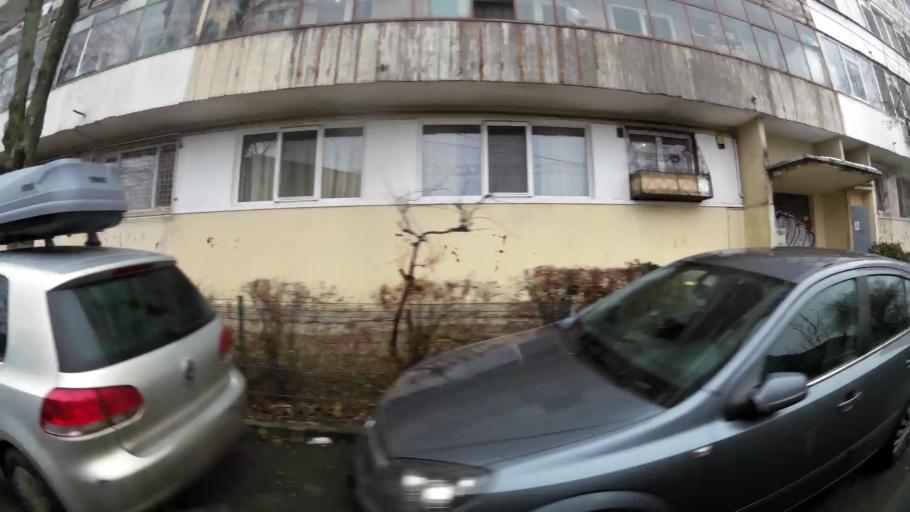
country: RO
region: Ilfov
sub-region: Comuna Chiajna
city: Rosu
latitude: 44.4594
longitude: 26.0501
